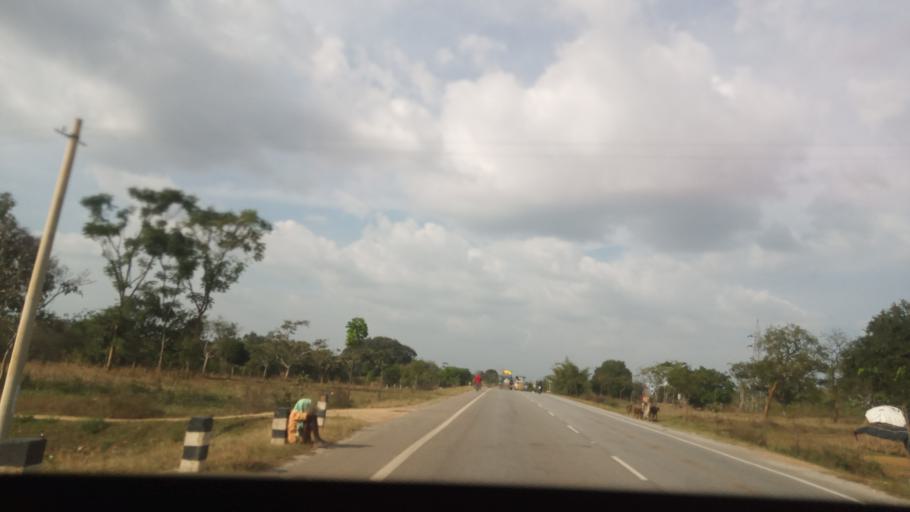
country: IN
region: Karnataka
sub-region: Tumkur
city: Kunigal
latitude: 12.8291
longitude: 77.0277
